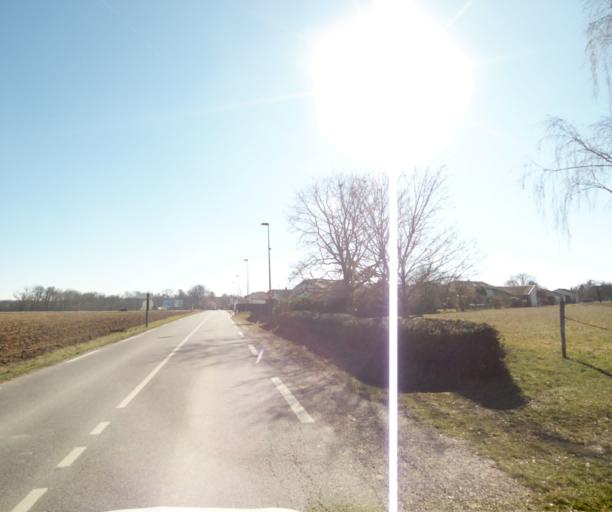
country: FR
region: Lorraine
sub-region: Departement de Meurthe-et-Moselle
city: Saulxures-les-Nancy
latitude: 48.6944
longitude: 6.2503
